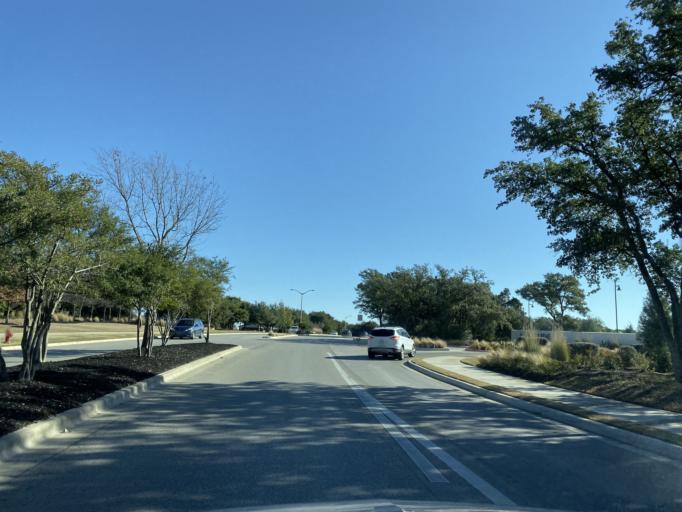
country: US
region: Texas
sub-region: Williamson County
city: Brushy Creek
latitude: 30.5232
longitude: -97.7732
